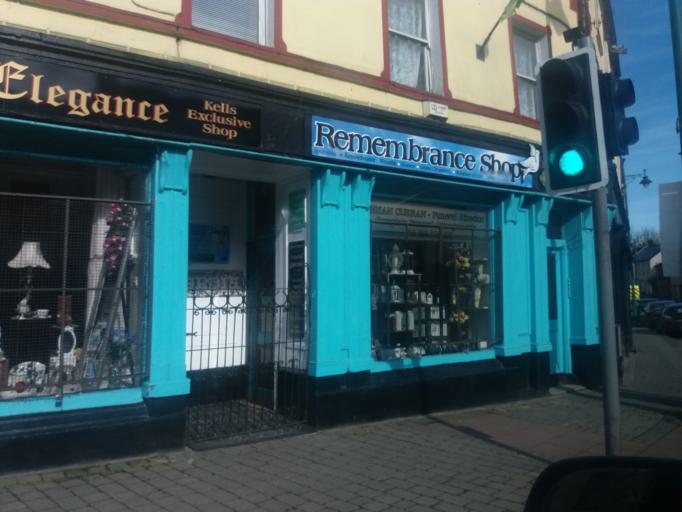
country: IE
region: Leinster
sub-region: An Mhi
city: Kells
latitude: 53.7275
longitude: -6.8769
